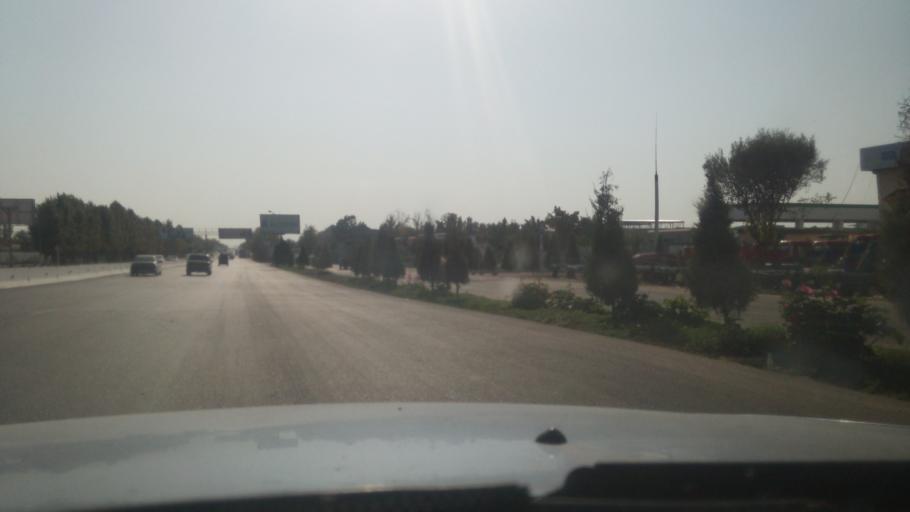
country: UZ
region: Toshkent
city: Urtaowul
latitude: 41.2310
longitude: 69.1525
